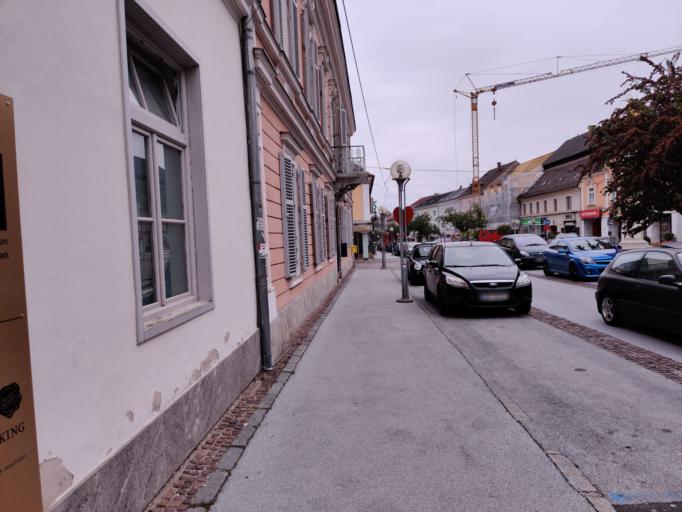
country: AT
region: Styria
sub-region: Politischer Bezirk Deutschlandsberg
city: Deutschlandsberg
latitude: 46.8148
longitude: 15.2136
